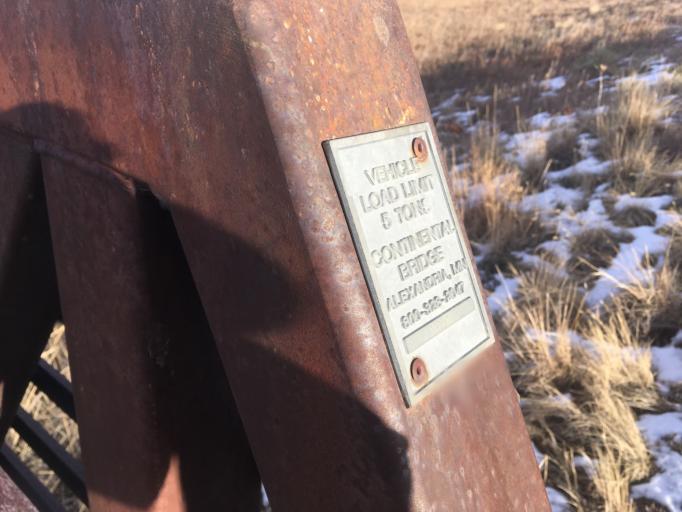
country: US
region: Colorado
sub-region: Broomfield County
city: Broomfield
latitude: 39.9320
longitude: -105.1087
